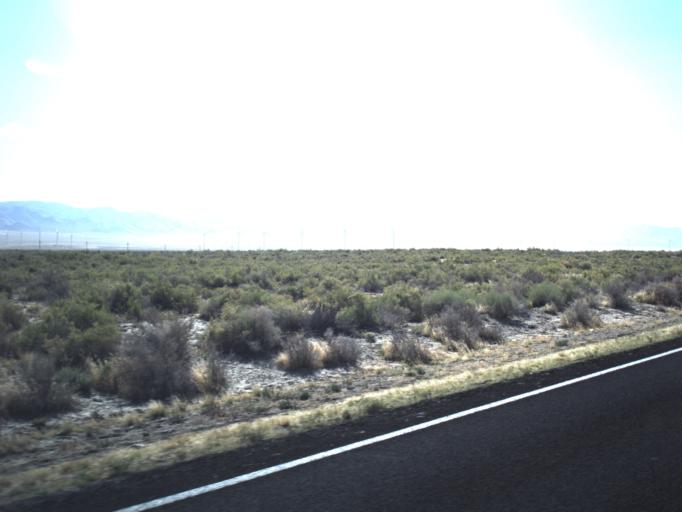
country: US
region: Utah
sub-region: Beaver County
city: Milford
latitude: 38.5578
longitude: -112.9912
